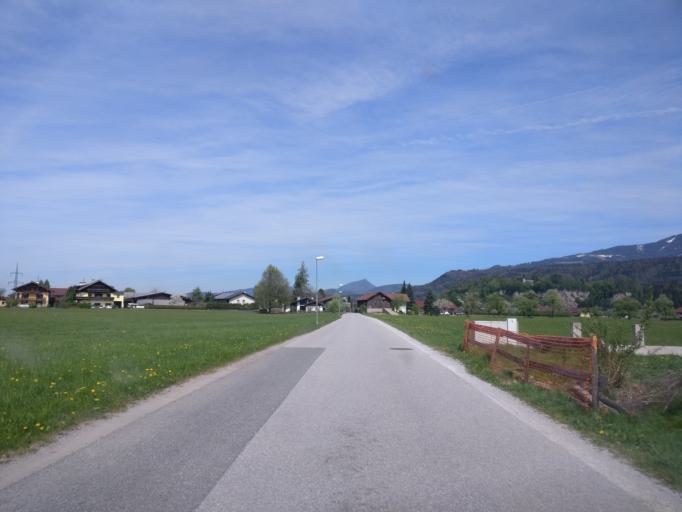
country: AT
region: Salzburg
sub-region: Politischer Bezirk Hallein
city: Kuchl
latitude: 47.6243
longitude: 13.1549
